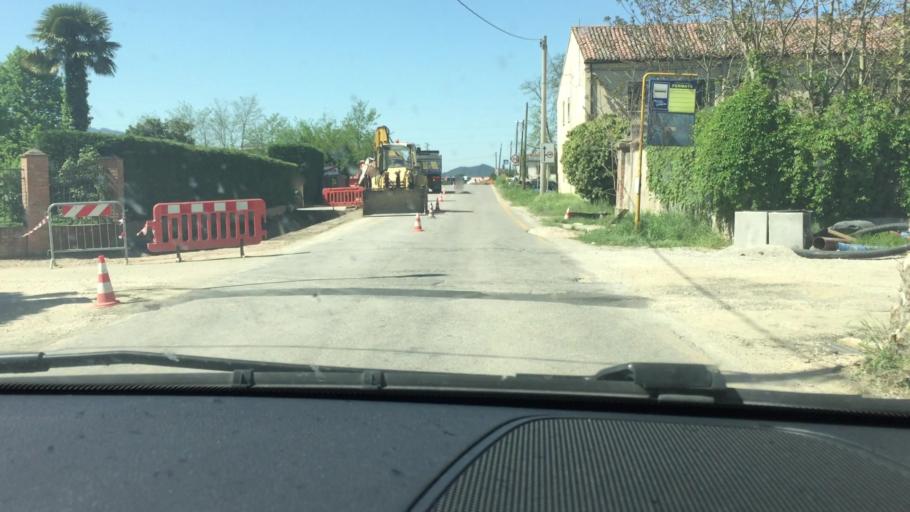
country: IT
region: Veneto
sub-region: Provincia di Padova
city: Pernumia
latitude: 45.2642
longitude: 11.7856
